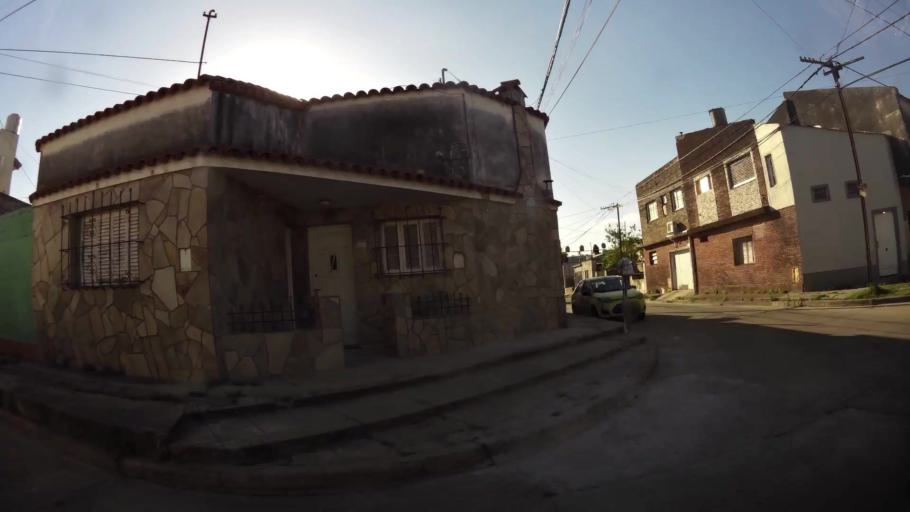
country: AR
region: Santa Fe
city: Santa Fe de la Vera Cruz
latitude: -31.6097
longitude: -60.6972
